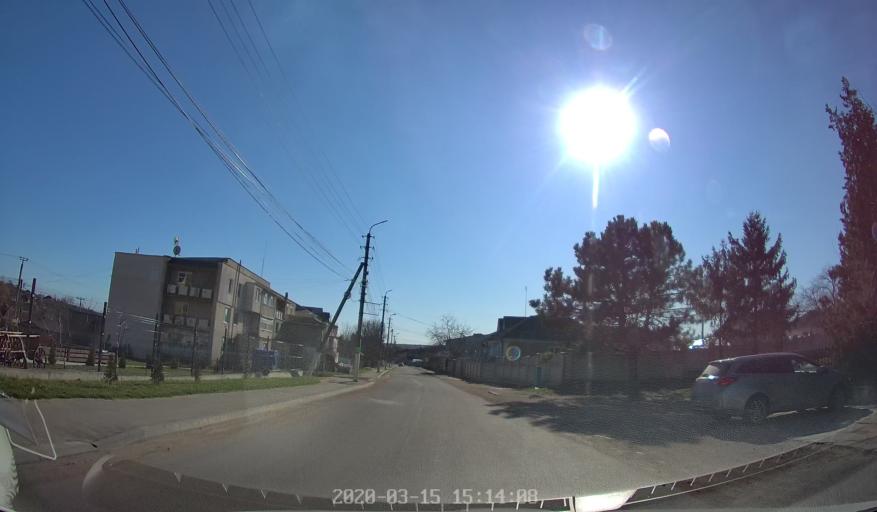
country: MD
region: Chisinau
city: Cricova
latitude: 47.2478
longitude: 28.7679
